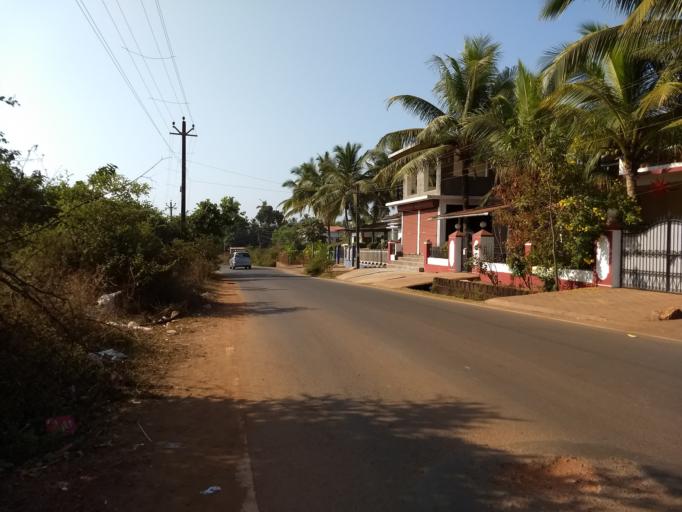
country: IN
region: Goa
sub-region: North Goa
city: Vagator
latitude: 15.5901
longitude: 73.7430
